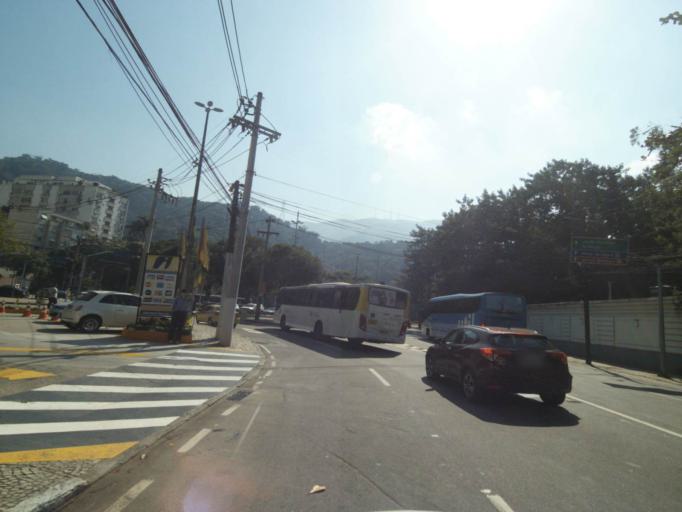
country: BR
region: Rio de Janeiro
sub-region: Rio De Janeiro
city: Rio de Janeiro
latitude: -22.9752
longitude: -43.2258
